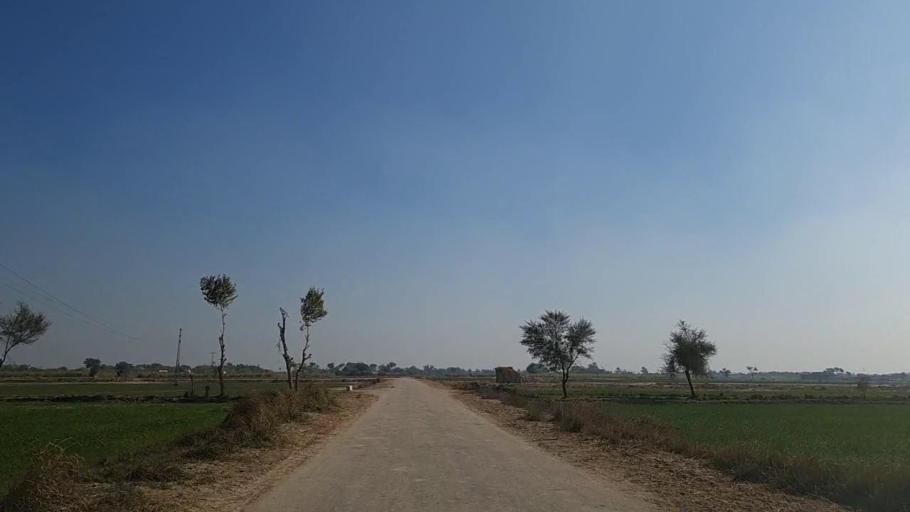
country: PK
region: Sindh
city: Daur
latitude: 26.4812
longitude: 68.3223
